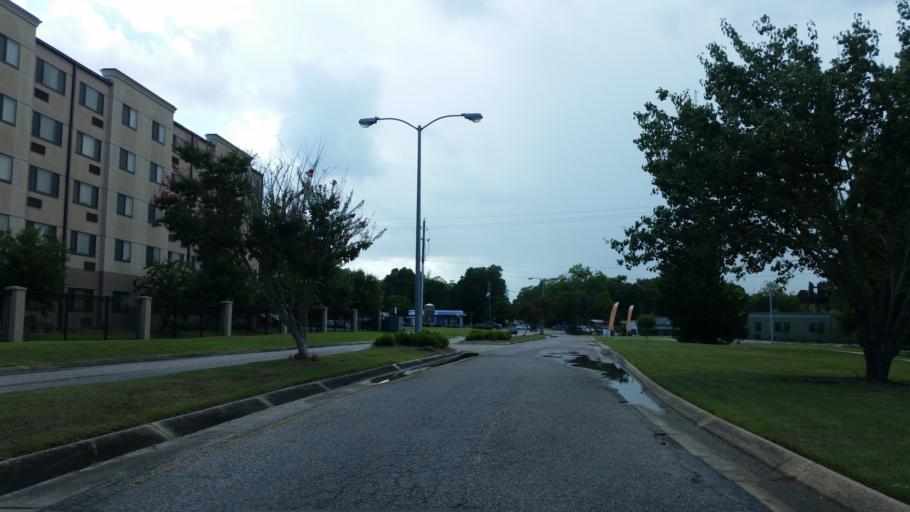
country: US
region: Florida
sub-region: Escambia County
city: Goulding
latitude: 30.4281
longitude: -87.2388
